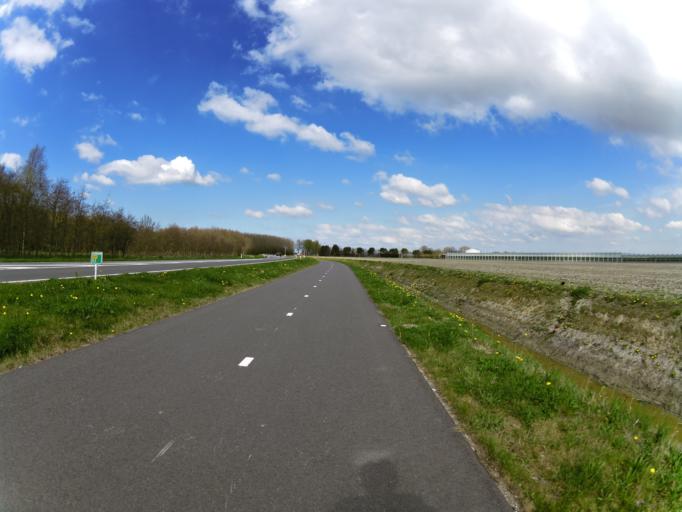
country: NL
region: South Holland
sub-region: Gemeente Brielle
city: Brielle
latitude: 51.8959
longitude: 4.1102
